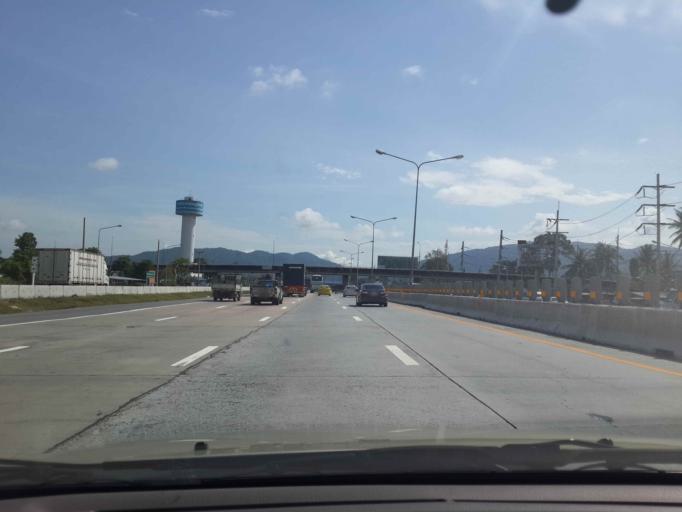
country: TH
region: Chon Buri
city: Si Racha
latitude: 13.2073
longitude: 101.0040
